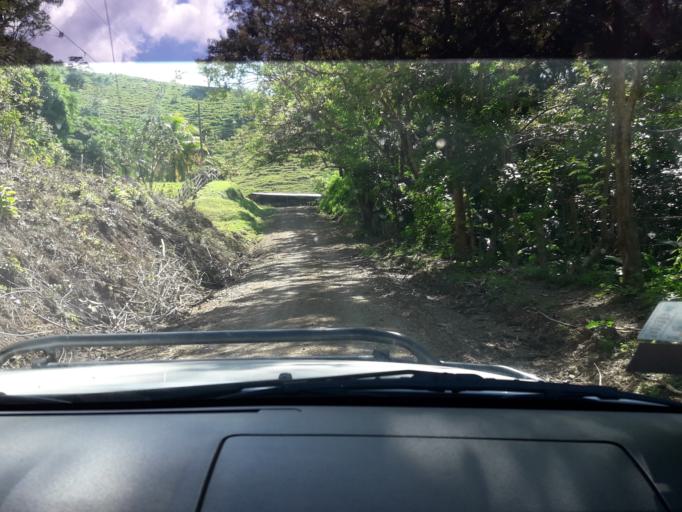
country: CR
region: Guanacaste
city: La Cruz
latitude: 11.1891
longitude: -85.6640
